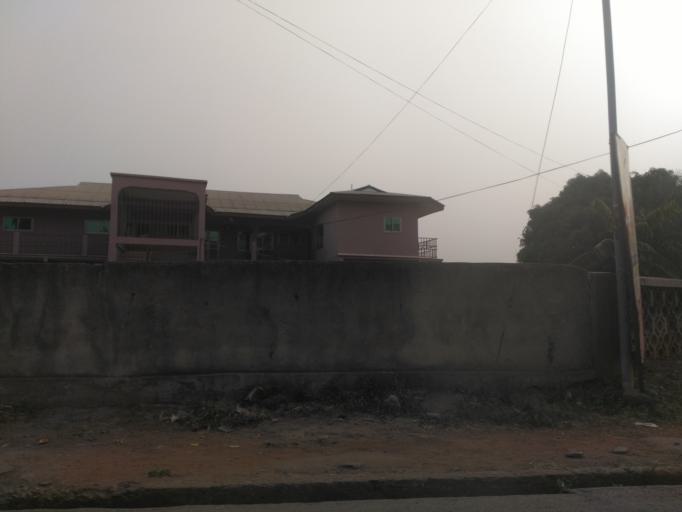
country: GH
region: Ashanti
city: Kumasi
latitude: 6.7087
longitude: -1.6091
